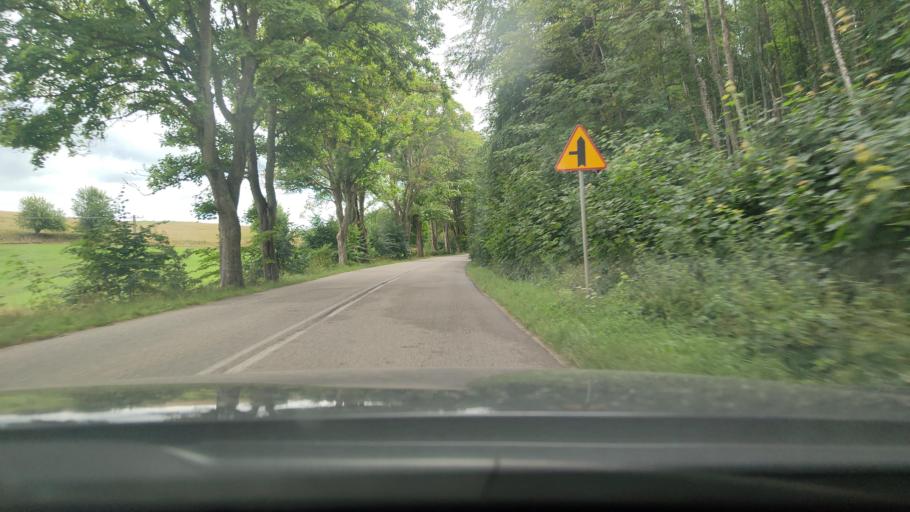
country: PL
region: Pomeranian Voivodeship
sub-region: Powiat pucki
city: Krokowa
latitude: 54.7549
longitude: 18.1730
